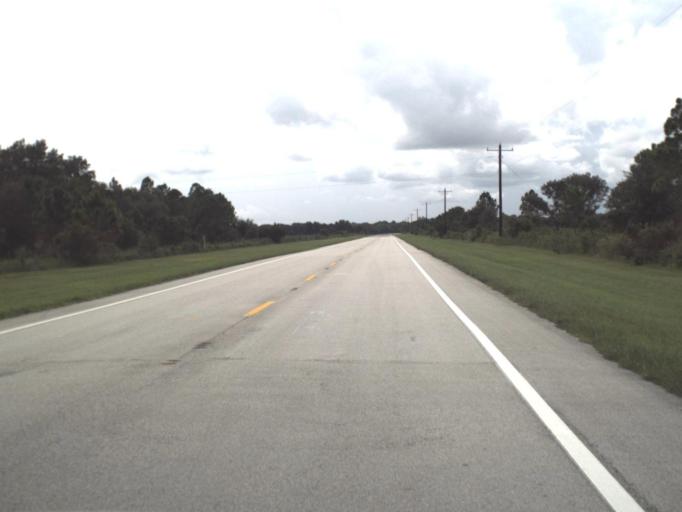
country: US
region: Florida
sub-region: DeSoto County
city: Nocatee
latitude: 27.2044
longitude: -82.0332
